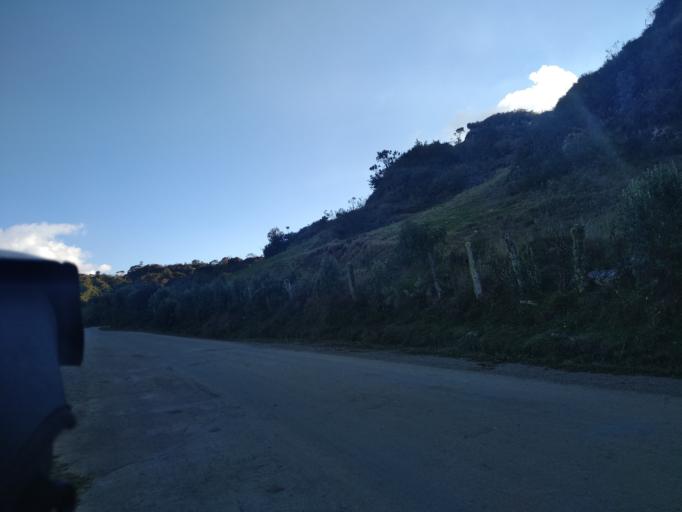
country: PE
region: Amazonas
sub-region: Provincia de Chachapoyas
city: Montevideo
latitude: -6.7162
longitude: -77.8649
